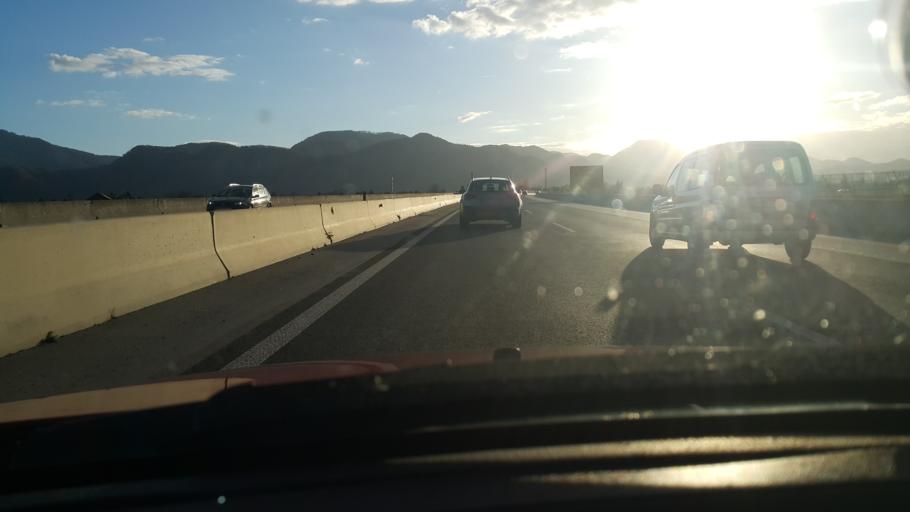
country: SI
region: Zalec
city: Sempeter v Savinj. Dolini
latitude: 46.2645
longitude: 15.1099
